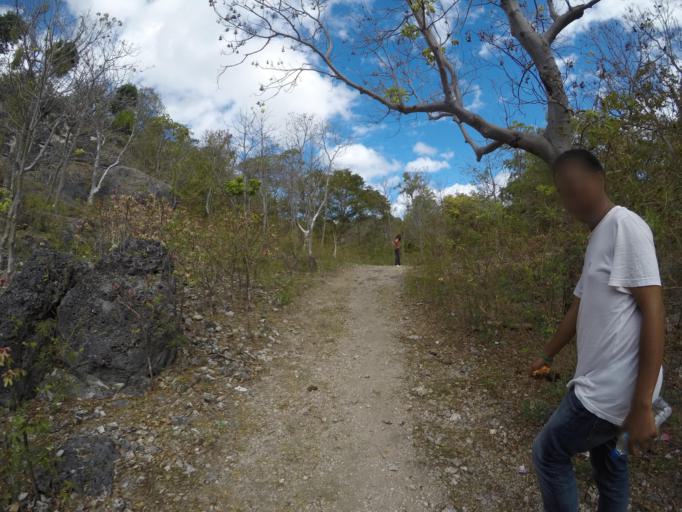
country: TL
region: Lautem
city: Lospalos
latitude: -8.3543
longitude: 127.0524
